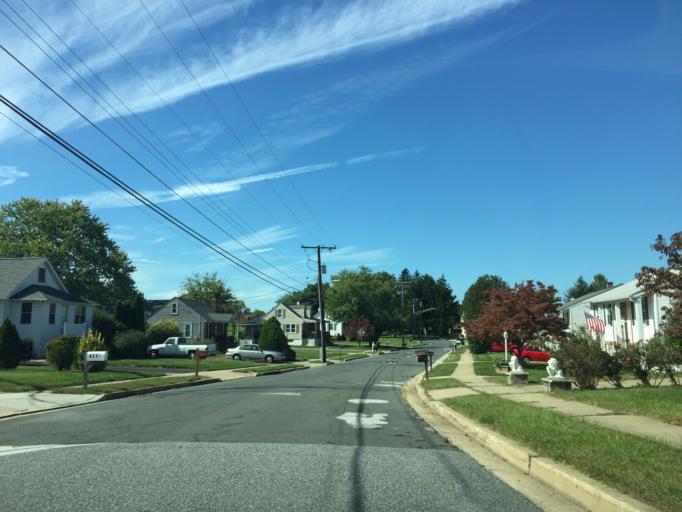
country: US
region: Maryland
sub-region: Baltimore County
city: Perry Hall
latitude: 39.4145
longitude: -76.4672
